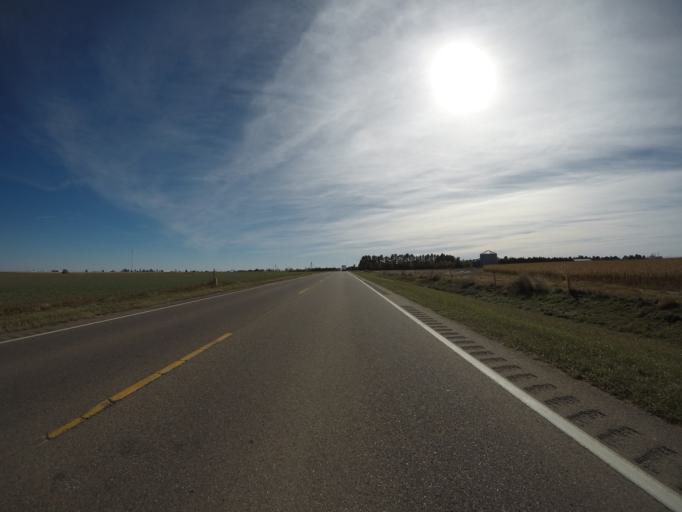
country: US
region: Colorado
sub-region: Kit Carson County
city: Burlington
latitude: 39.3204
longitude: -102.2601
